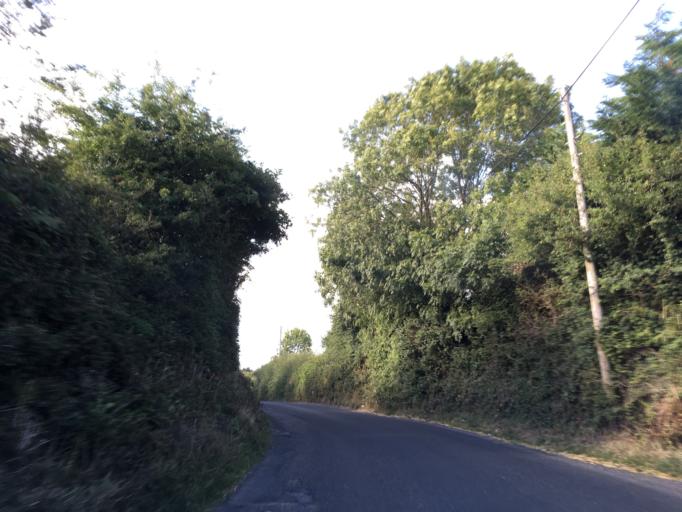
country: IE
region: Munster
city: Cahir
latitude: 52.2712
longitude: -7.9561
